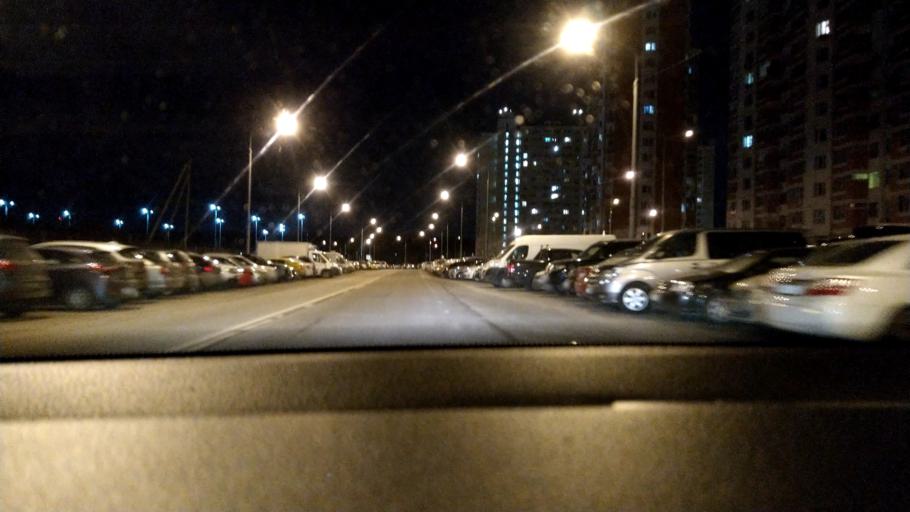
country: RU
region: Moscow
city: Novo-Peredelkino
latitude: 55.6415
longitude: 37.3266
